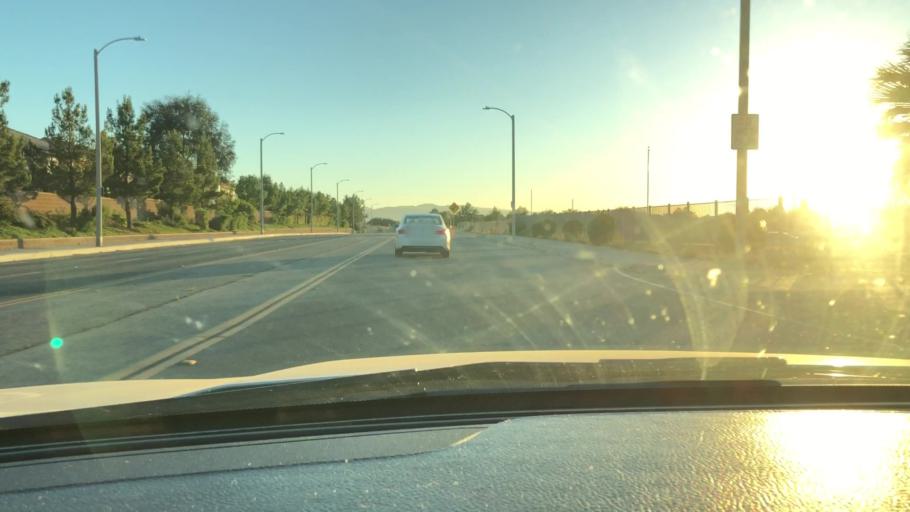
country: US
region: California
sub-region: Los Angeles County
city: Quartz Hill
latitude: 34.6824
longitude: -118.1900
